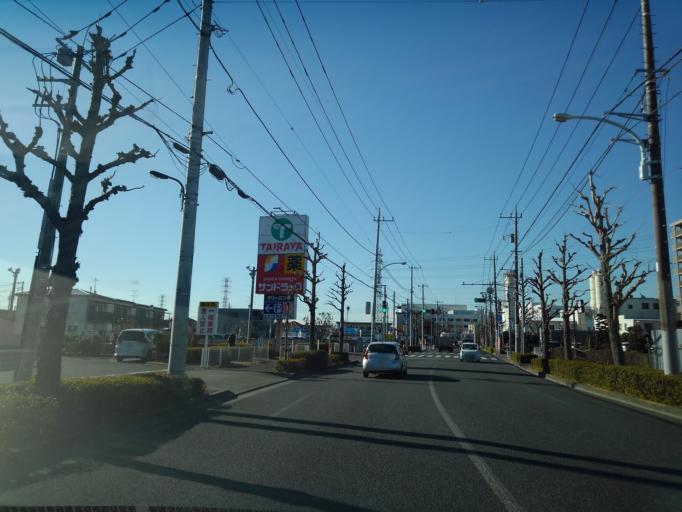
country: JP
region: Tokyo
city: Hino
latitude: 35.7202
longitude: 139.3834
